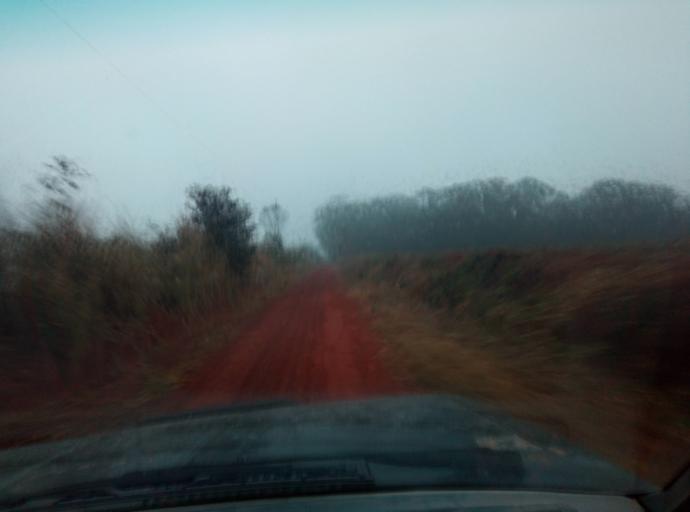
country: PY
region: Caaguazu
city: Doctor Cecilio Baez
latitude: -25.1585
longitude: -56.2669
